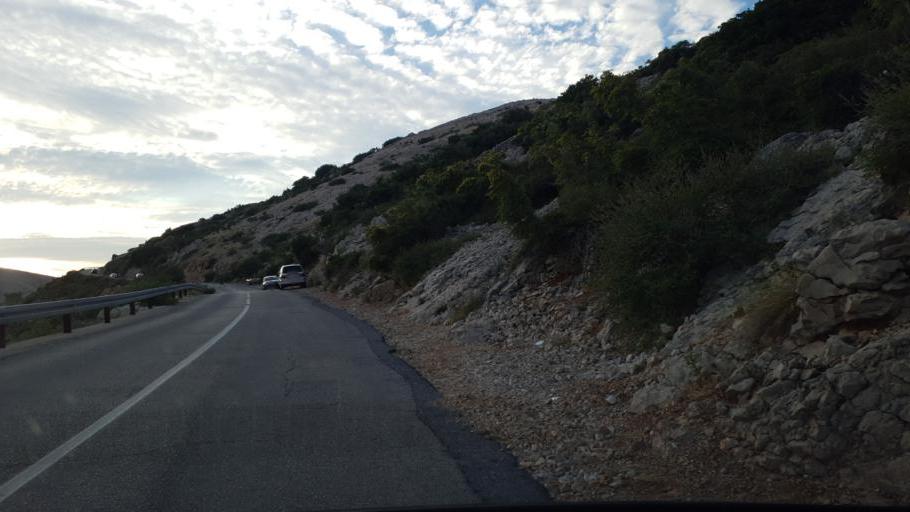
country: HR
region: Primorsko-Goranska
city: Punat
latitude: 44.9668
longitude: 14.6678
